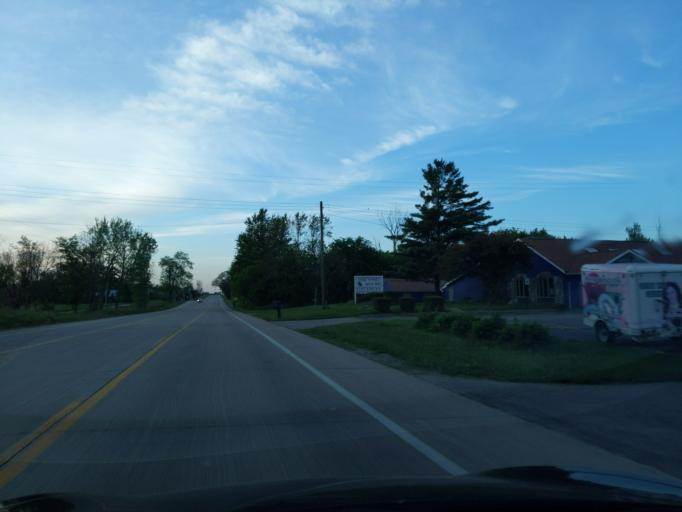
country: US
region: Michigan
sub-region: Ingham County
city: Okemos
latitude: 42.6704
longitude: -84.4329
